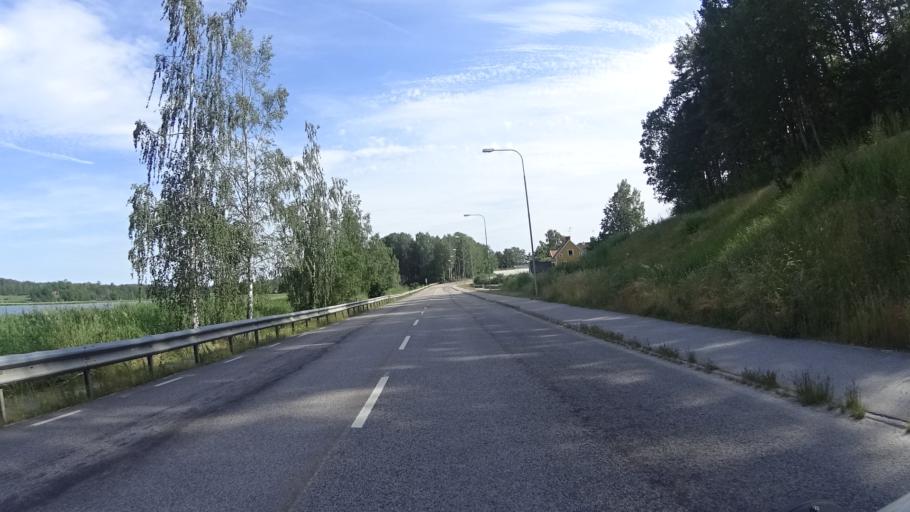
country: SE
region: Kalmar
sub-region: Vasterviks Kommun
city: Gamleby
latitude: 57.8939
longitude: 16.4153
